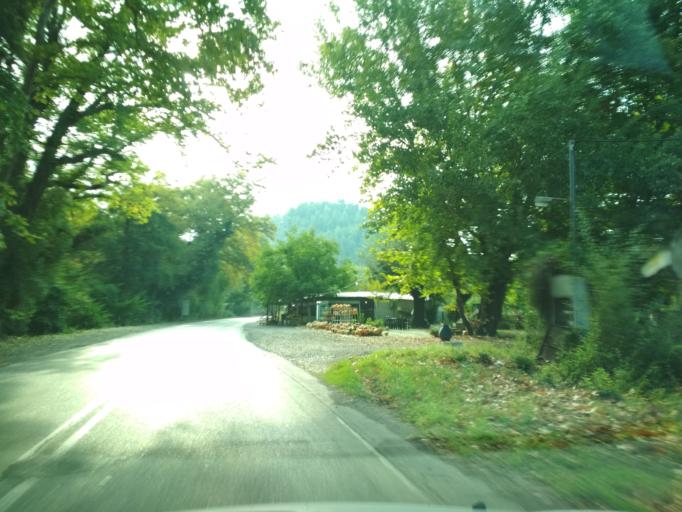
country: GR
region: Central Greece
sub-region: Nomos Evvoias
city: Mantoudi
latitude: 38.7765
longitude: 23.4716
